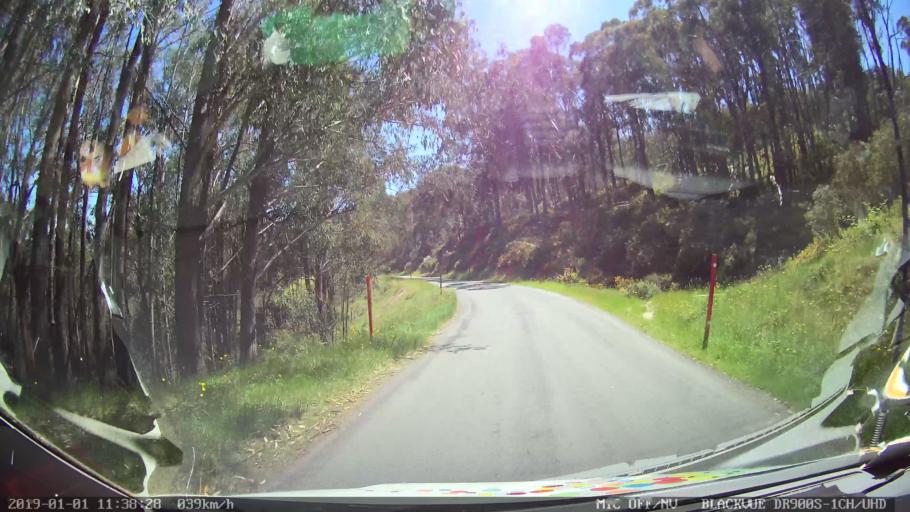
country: AU
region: New South Wales
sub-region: Snowy River
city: Jindabyne
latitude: -35.9342
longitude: 148.3868
